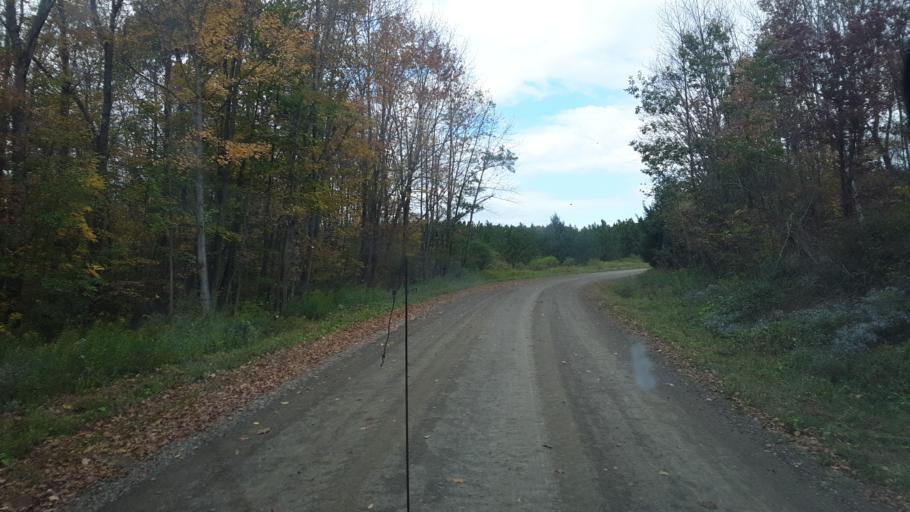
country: US
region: New York
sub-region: Allegany County
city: Alfred
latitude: 42.3829
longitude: -77.8603
